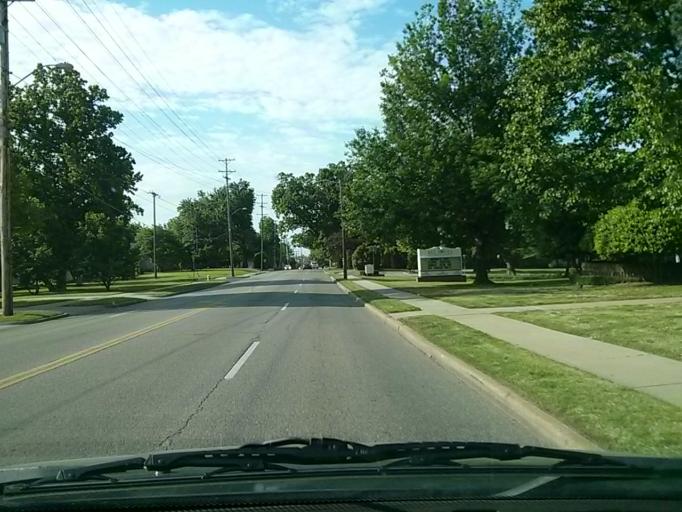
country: US
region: Oklahoma
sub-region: Tulsa County
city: Tulsa
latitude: 36.1214
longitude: -95.9757
